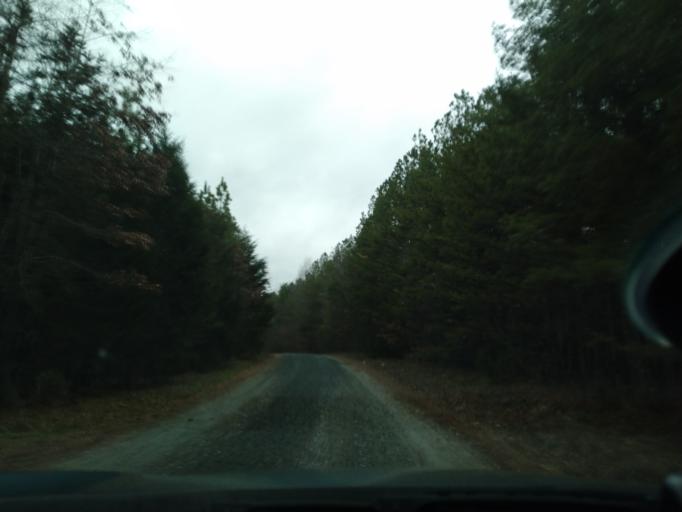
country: US
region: Virginia
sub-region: Buckingham County
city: Buckingham
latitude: 37.4326
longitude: -78.6553
